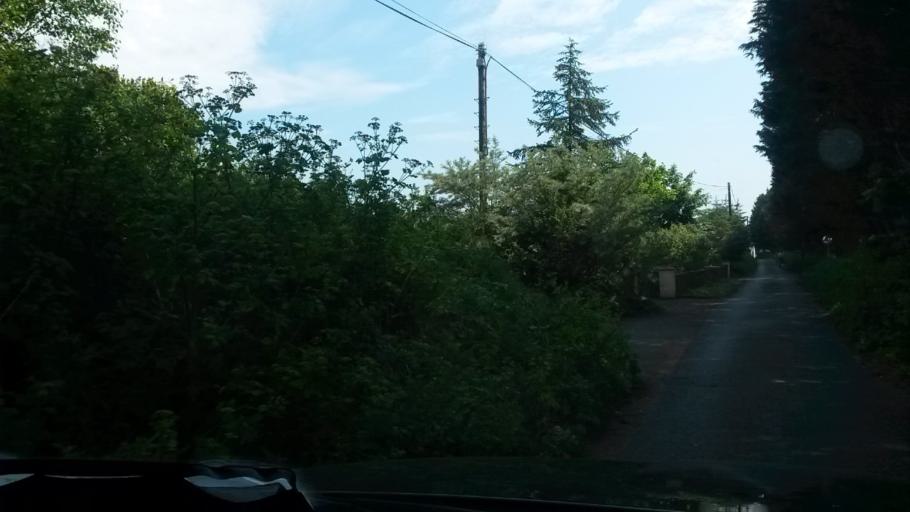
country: IE
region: Leinster
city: Portraine
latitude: 53.5071
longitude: -6.1259
